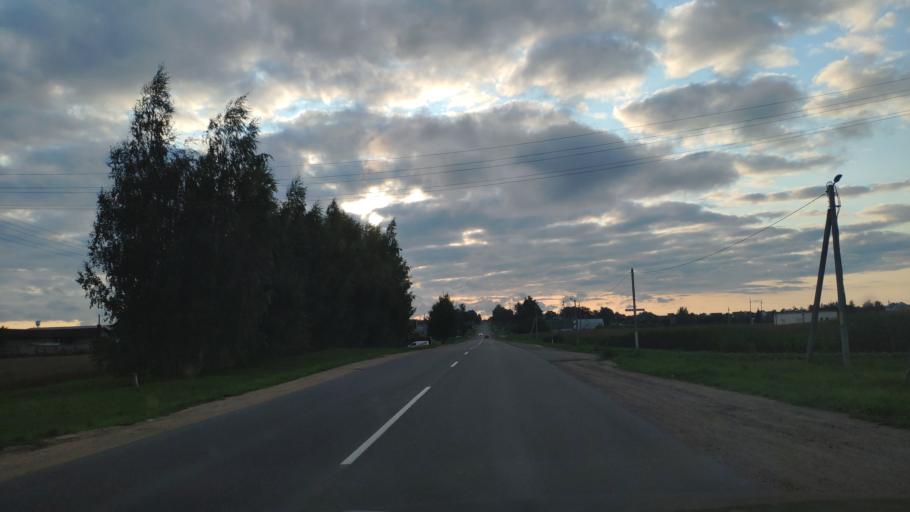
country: BY
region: Minsk
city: Azyartso
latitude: 53.8387
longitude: 27.3764
